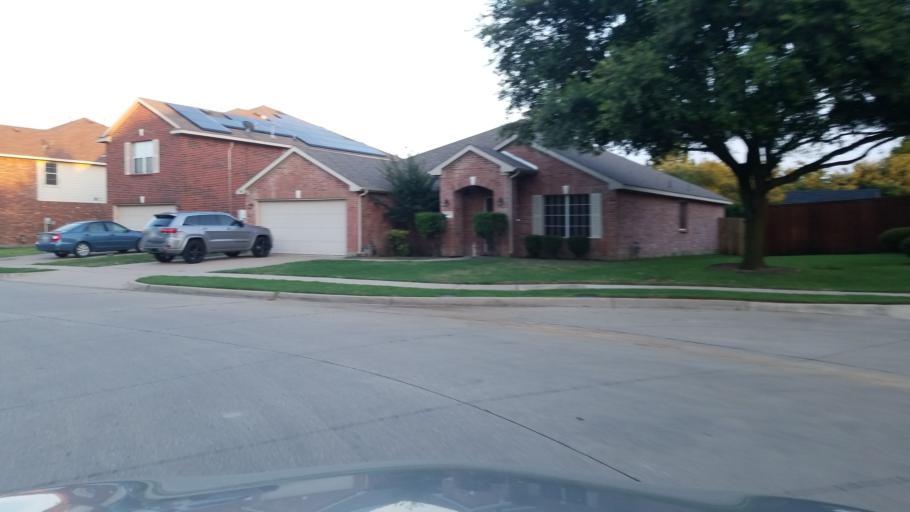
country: US
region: Texas
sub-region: Dallas County
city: Grand Prairie
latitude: 32.6846
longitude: -97.0416
